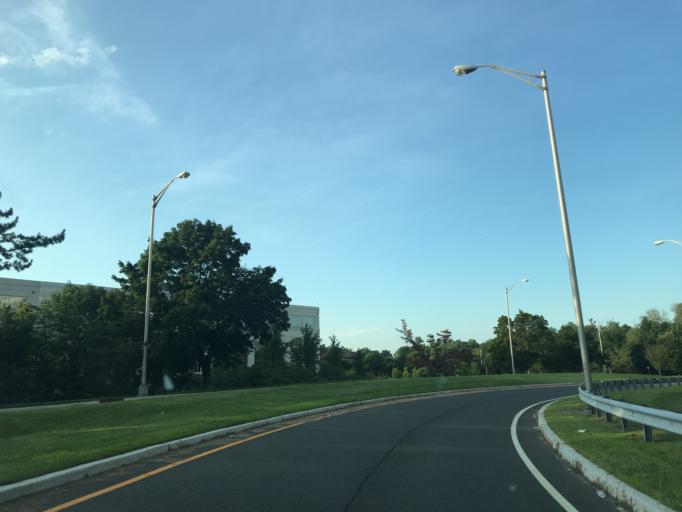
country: US
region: New Jersey
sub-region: Morris County
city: Parsippany
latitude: 40.8394
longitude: -74.4523
